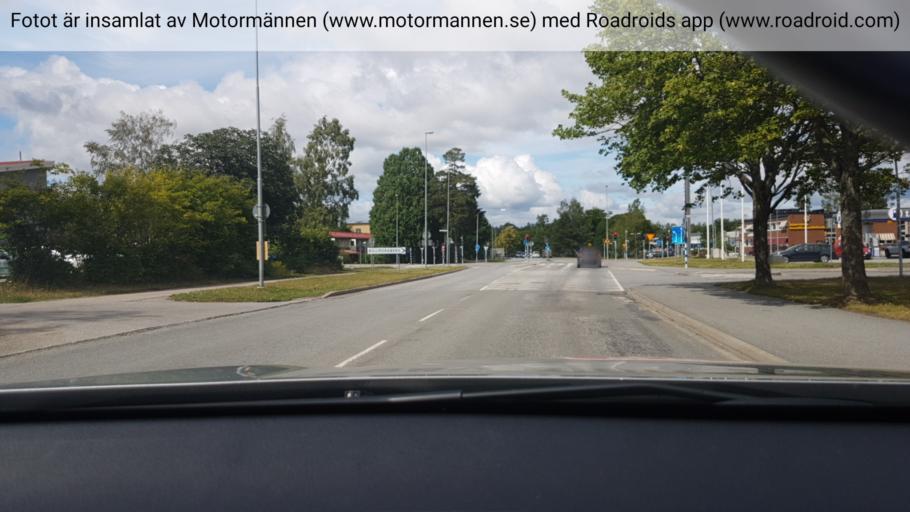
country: SE
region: Stockholm
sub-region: Tyreso Kommun
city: Bollmora
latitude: 59.2419
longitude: 18.2148
